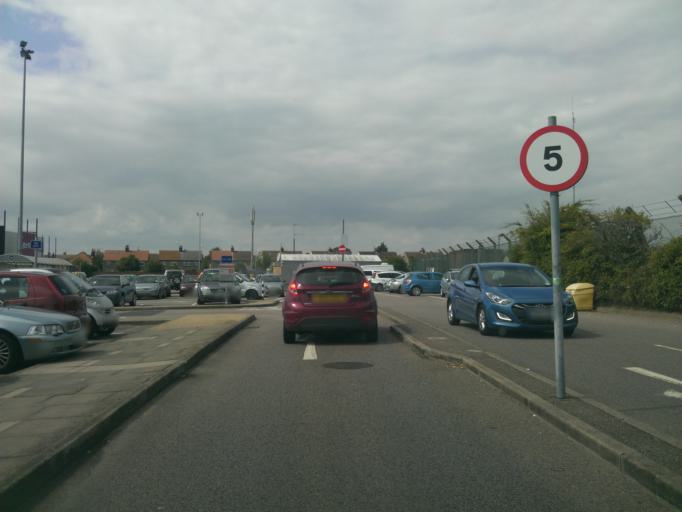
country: GB
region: England
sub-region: Essex
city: Clacton-on-Sea
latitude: 51.7906
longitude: 1.1475
